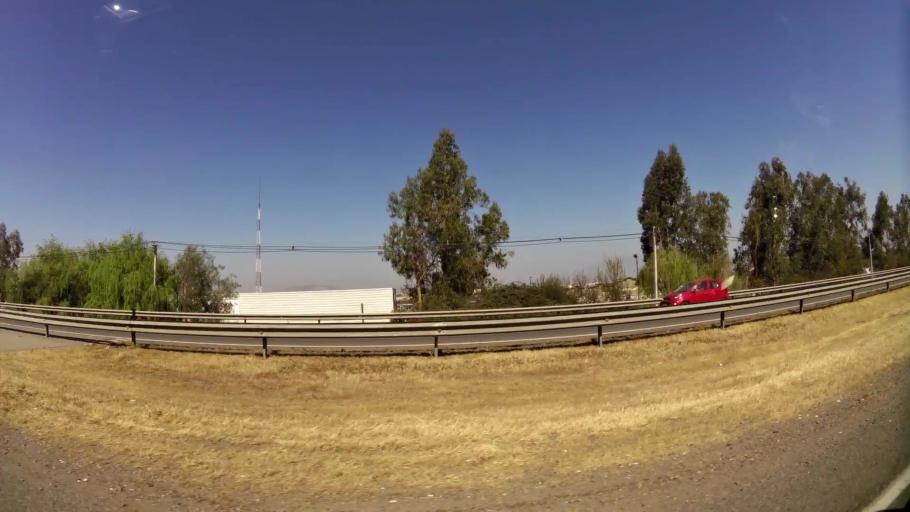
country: CL
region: Santiago Metropolitan
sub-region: Provincia de Chacabuco
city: Chicureo Abajo
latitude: -33.3309
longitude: -70.6971
